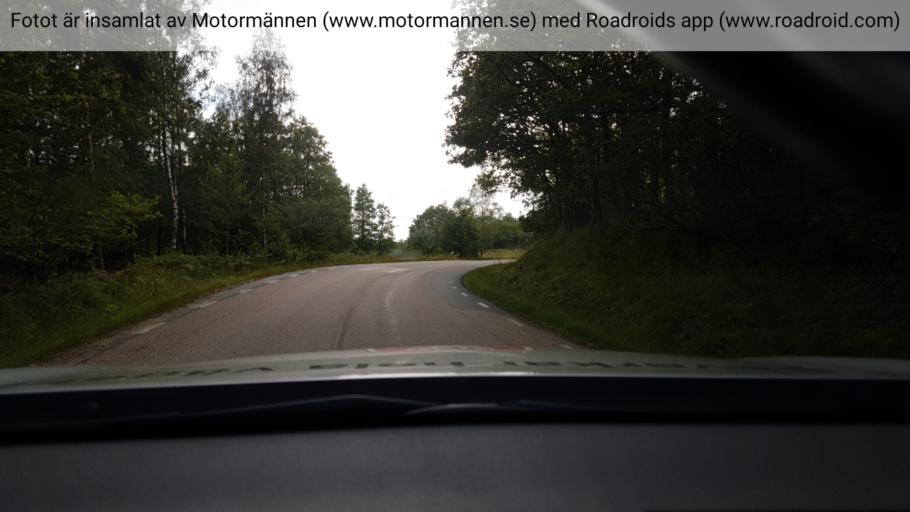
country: SE
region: Vaestra Goetaland
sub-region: Orust
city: Henan
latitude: 58.1592
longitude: 11.6621
